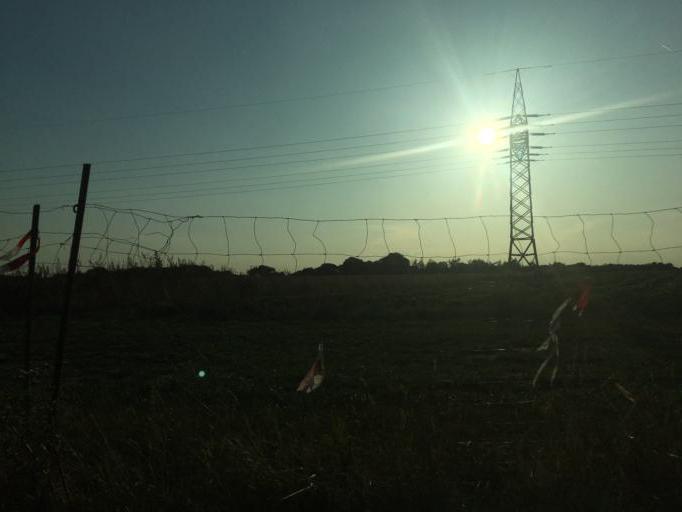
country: DE
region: Saxony
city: Wilsdruff
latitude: 51.0704
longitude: 13.5954
